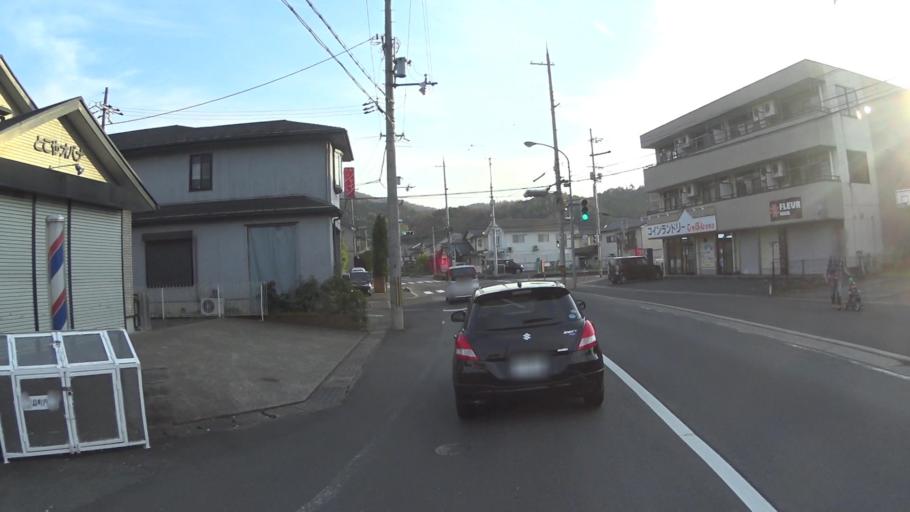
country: JP
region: Kyoto
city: Maizuru
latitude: 35.4840
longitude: 135.4335
